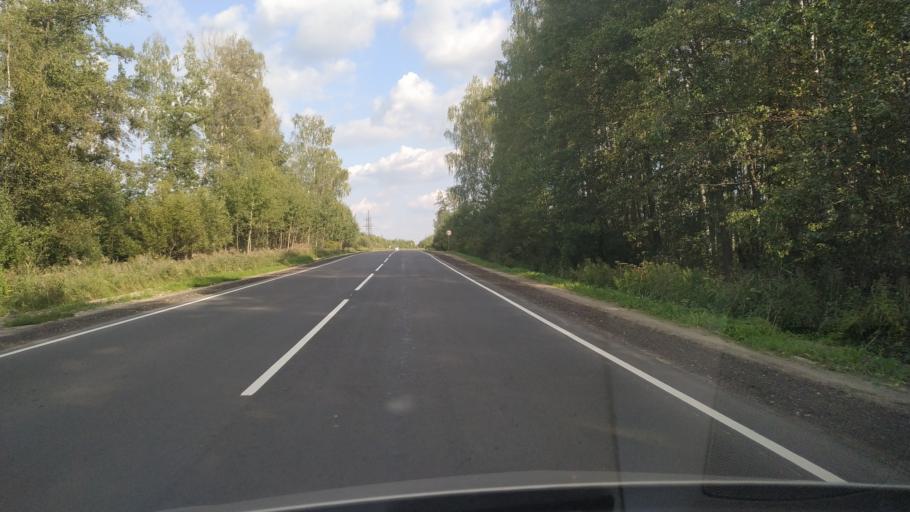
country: RU
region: Moskovskaya
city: Vereya
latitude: 55.7260
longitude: 39.0414
